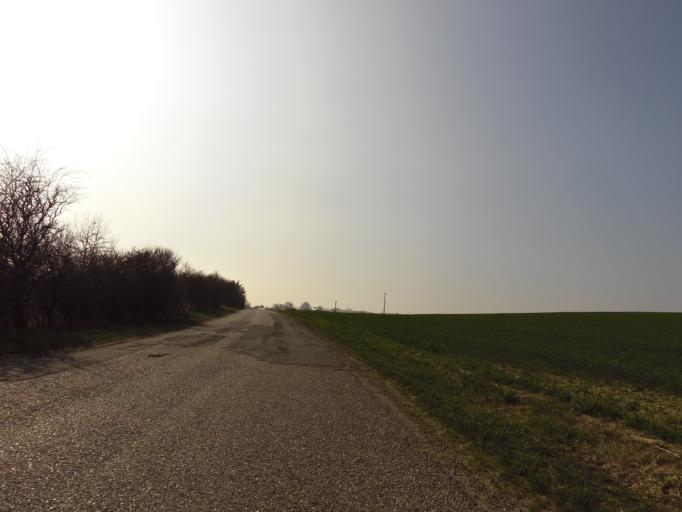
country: DK
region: Central Jutland
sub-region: Holstebro Kommune
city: Vinderup
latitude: 56.4339
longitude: 8.7863
